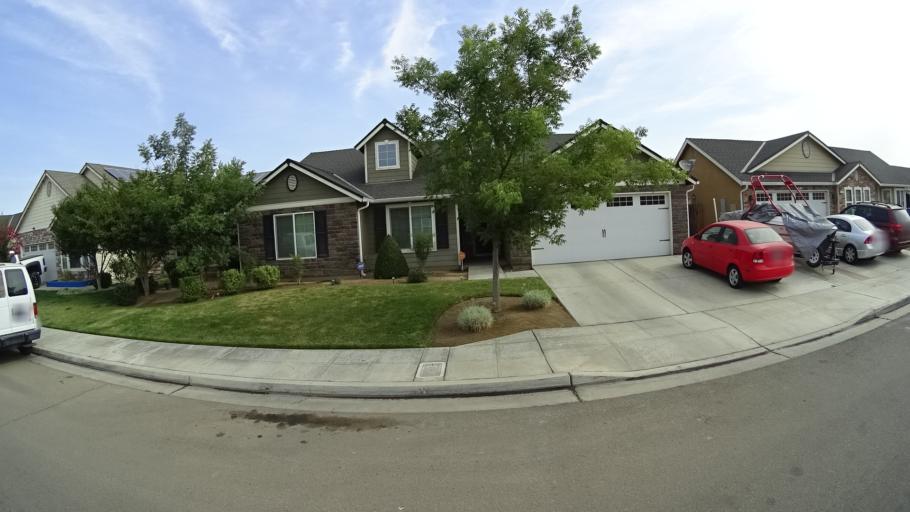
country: US
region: California
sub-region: Fresno County
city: West Park
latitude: 36.7741
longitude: -119.8771
